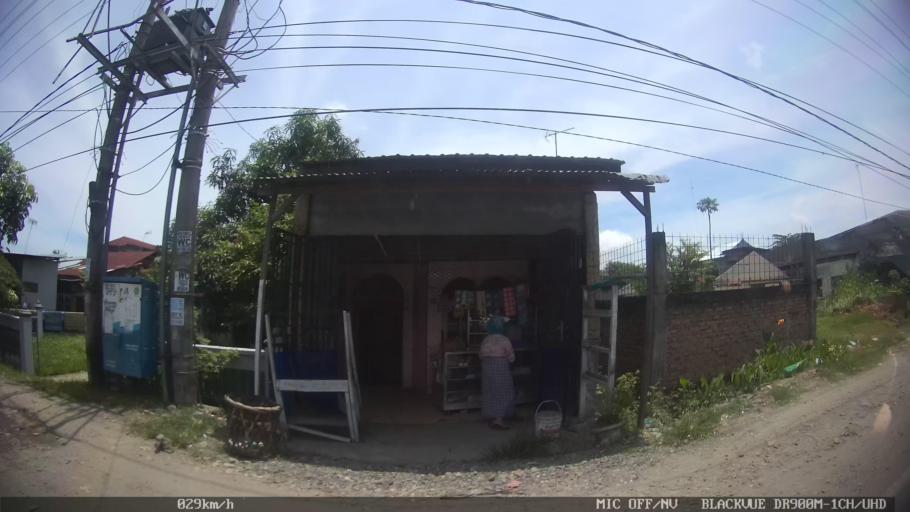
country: ID
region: North Sumatra
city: Labuhan Deli
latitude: 3.7434
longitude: 98.6748
